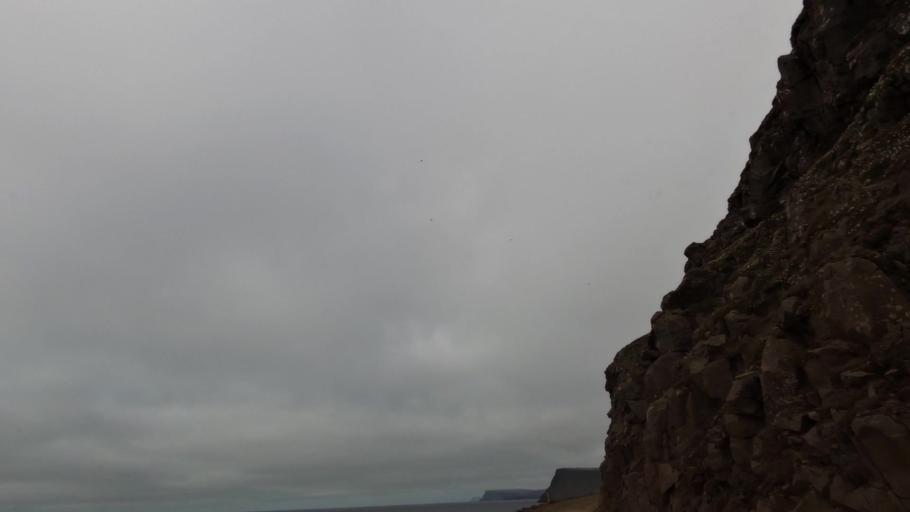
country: IS
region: West
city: Olafsvik
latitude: 65.5108
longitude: -24.5094
